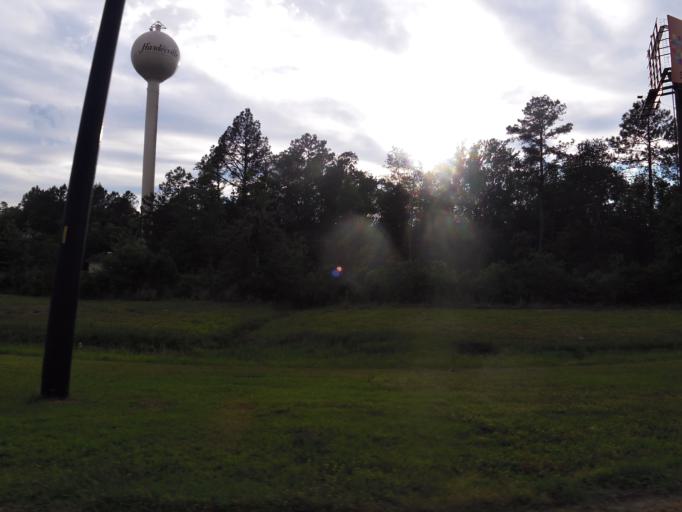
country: US
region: South Carolina
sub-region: Jasper County
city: Hardeeville
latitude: 32.2725
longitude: -81.0827
